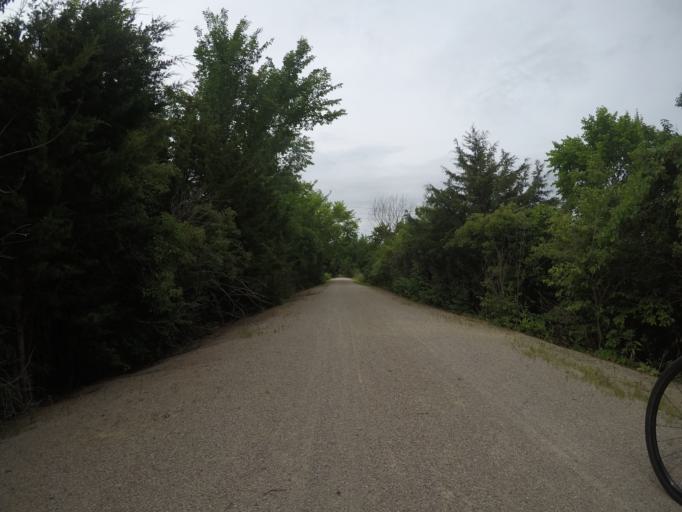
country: US
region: Kansas
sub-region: Franklin County
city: Ottawa
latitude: 38.5730
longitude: -95.2710
